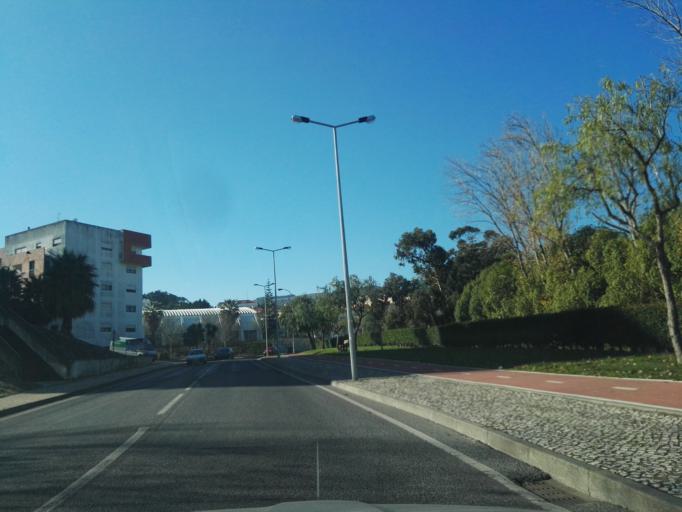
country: PT
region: Lisbon
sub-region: Arruda Dos Vinhos
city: Arruda dos Vinhos
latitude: 38.9803
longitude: -9.0786
